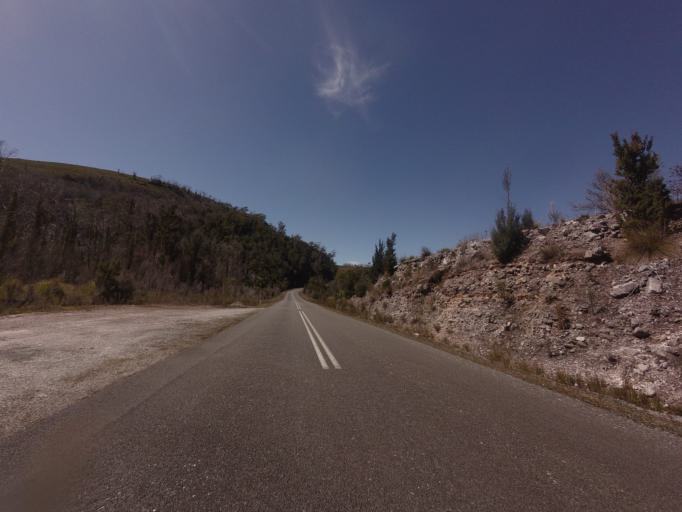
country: AU
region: Tasmania
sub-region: Huon Valley
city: Geeveston
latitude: -42.8596
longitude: 146.2289
